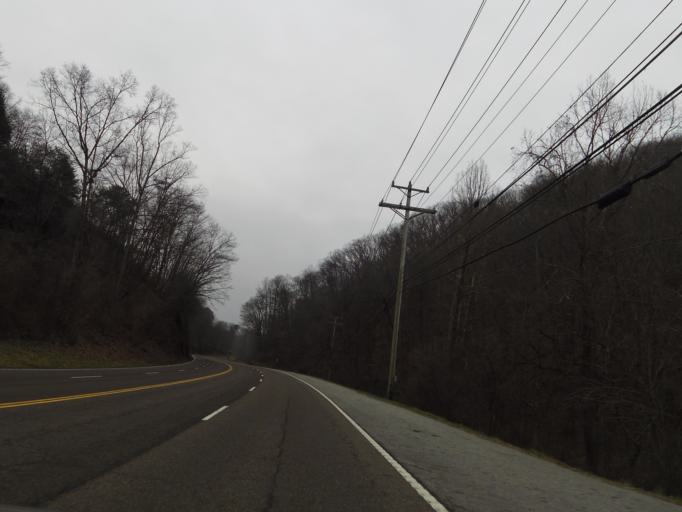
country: US
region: Tennessee
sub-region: Anderson County
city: Clinton
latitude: 36.0672
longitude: -84.1324
